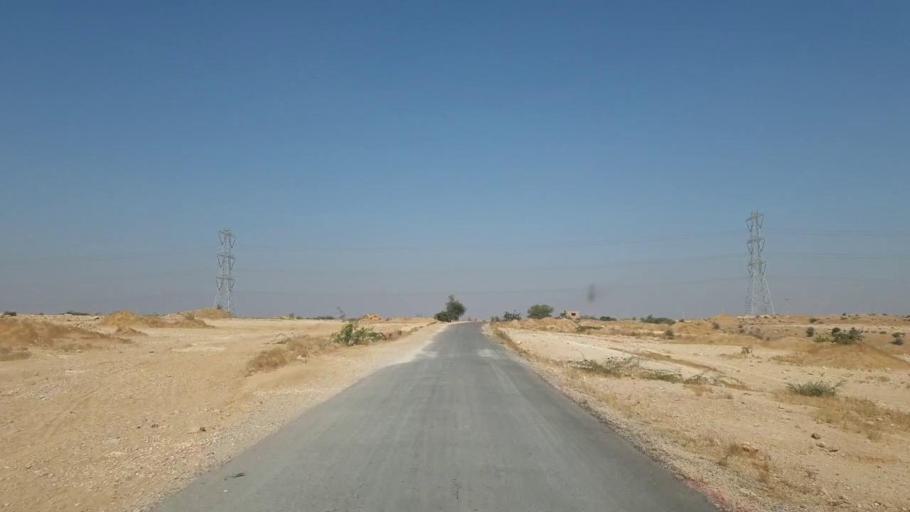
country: PK
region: Sindh
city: Thatta
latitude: 25.2000
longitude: 67.7978
